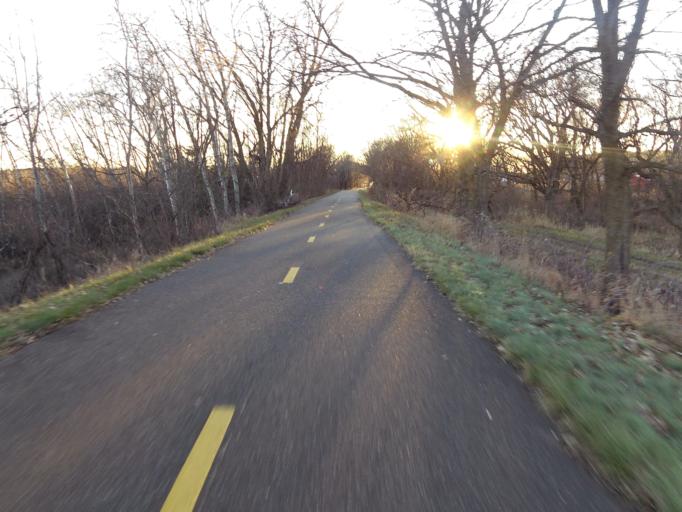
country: US
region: Minnesota
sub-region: Washington County
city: Grant
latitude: 45.1078
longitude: -92.8606
